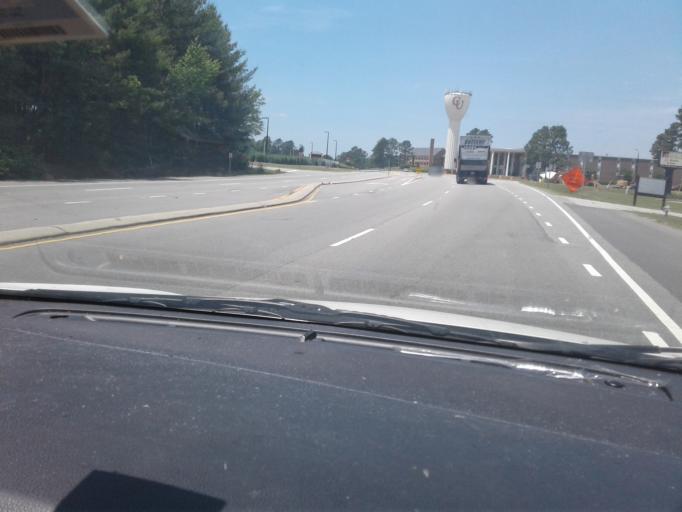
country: US
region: North Carolina
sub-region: Harnett County
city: Buies Creek
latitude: 35.4013
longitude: -78.7359
